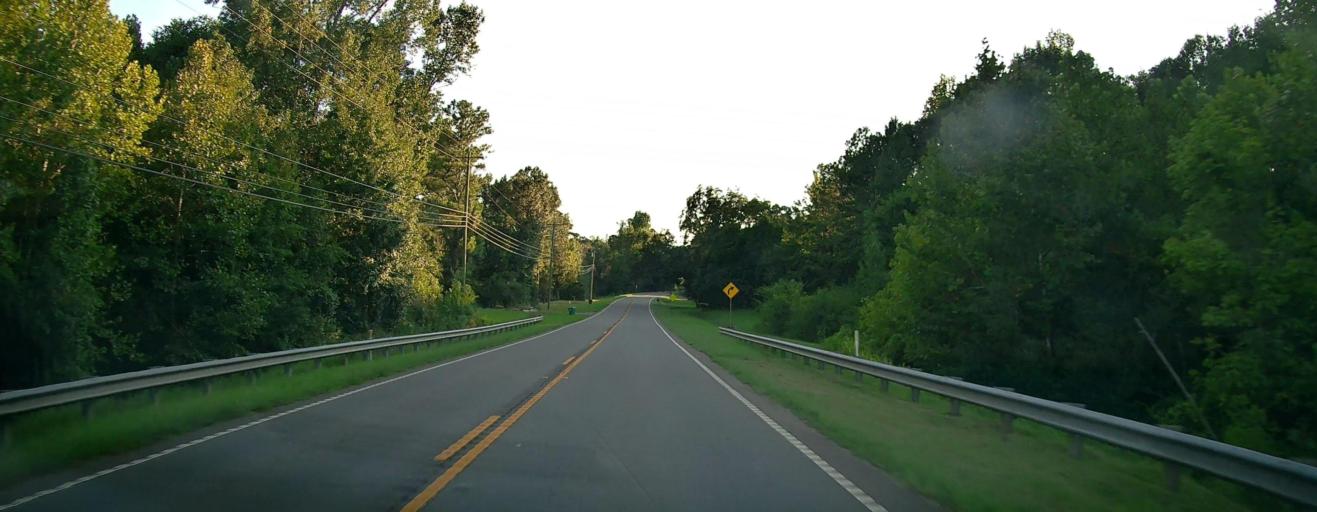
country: US
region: Georgia
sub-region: Crawford County
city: Roberta
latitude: 32.7040
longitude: -84.0355
